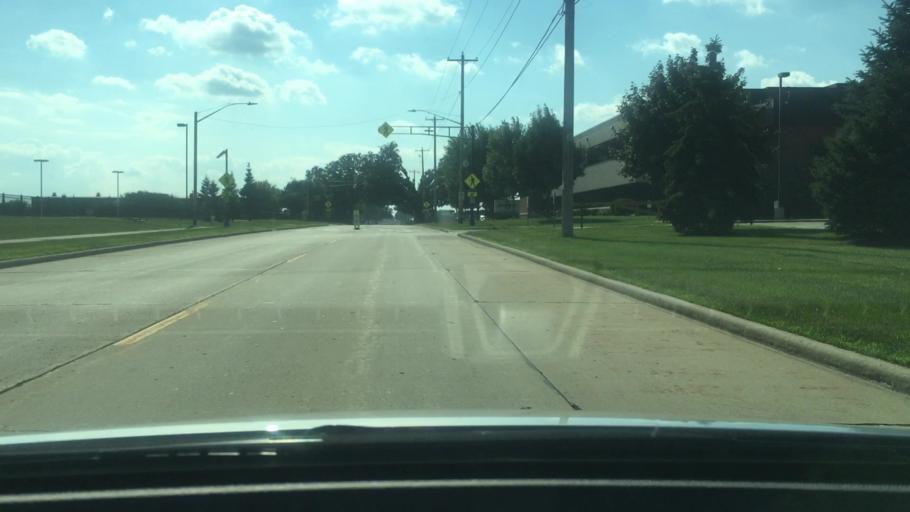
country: US
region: Wisconsin
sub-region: Winnebago County
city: Oshkosh
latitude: 43.9812
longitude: -88.5449
